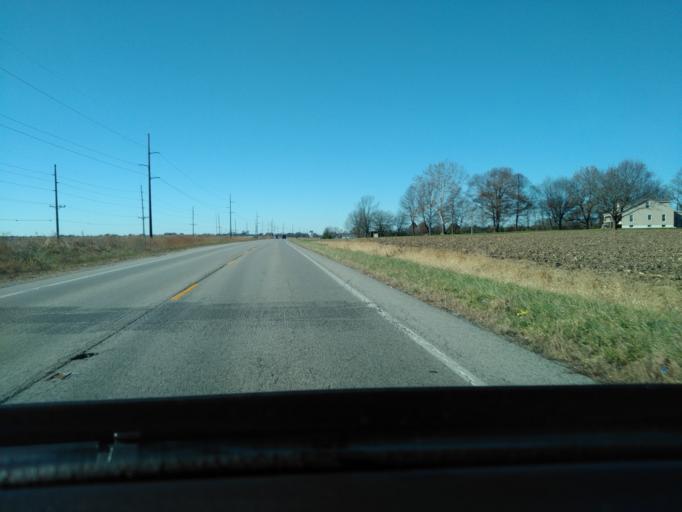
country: US
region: Illinois
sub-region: Madison County
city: Saint Jacob
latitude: 38.7271
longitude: -89.7380
